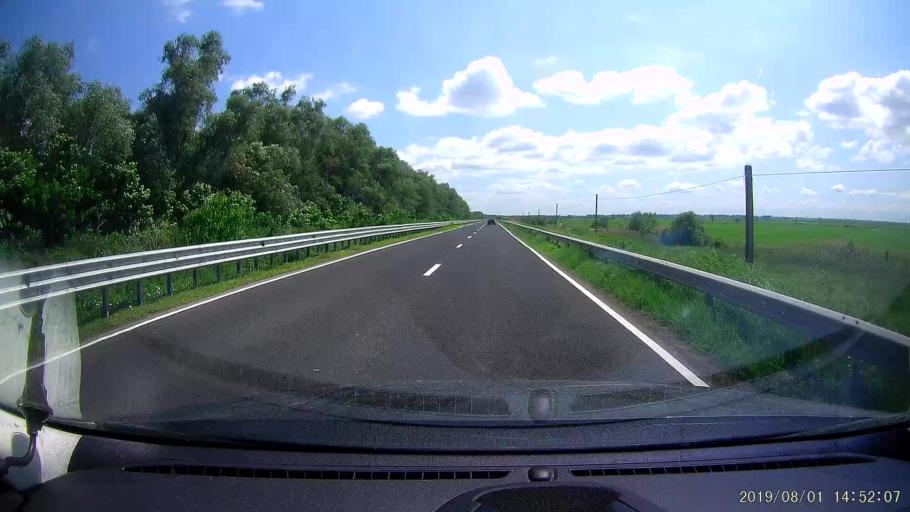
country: RO
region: Braila
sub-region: Comuna Vadeni
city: Vadeni
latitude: 45.3620
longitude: 28.0129
